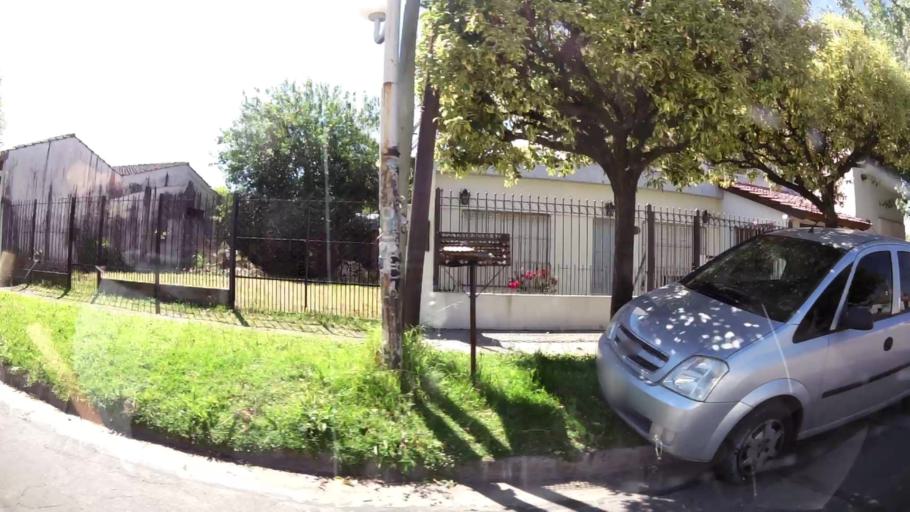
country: AR
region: Buenos Aires
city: Ituzaingo
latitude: -34.6645
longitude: -58.6502
